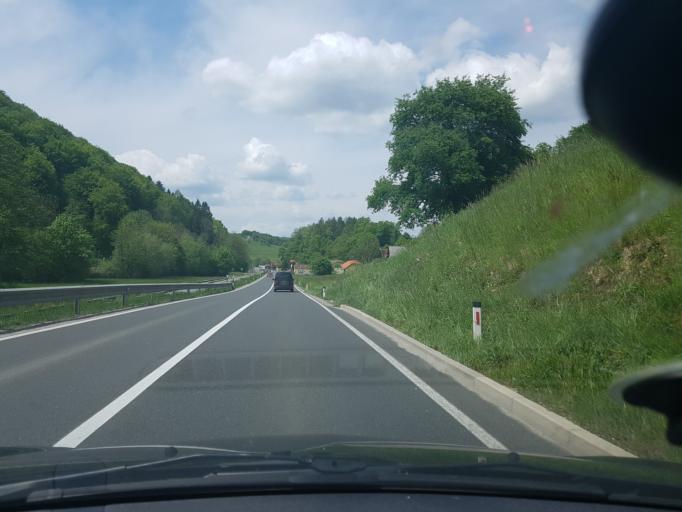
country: SI
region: Rogaska Slatina
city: Rogaska Slatina
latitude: 46.2424
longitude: 15.5826
